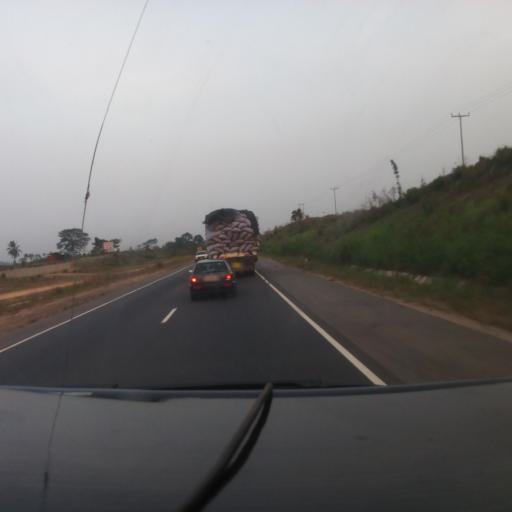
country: GH
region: Eastern
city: Nsawam
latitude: 5.8890
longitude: -0.3805
